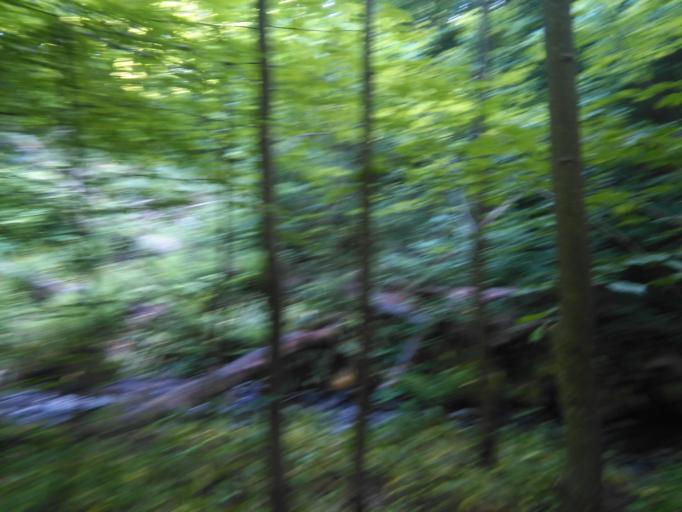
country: DK
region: Capital Region
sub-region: Bornholm Kommune
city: Akirkeby
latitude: 55.2231
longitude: 14.8801
